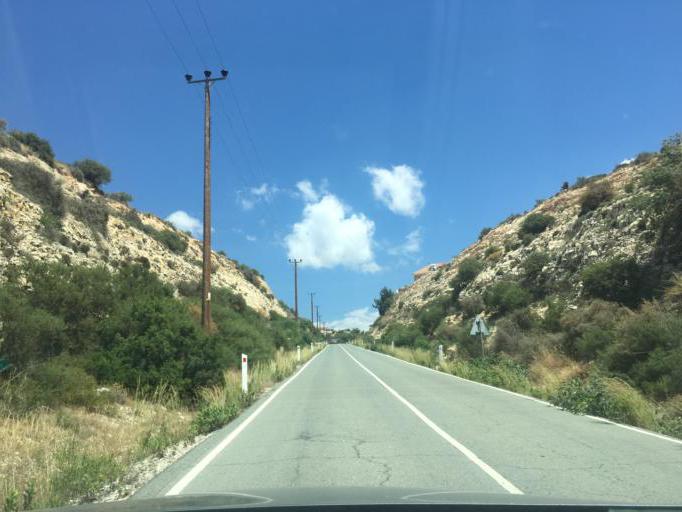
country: CY
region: Limassol
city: Mouttagiaka
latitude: 34.7496
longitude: 33.0566
